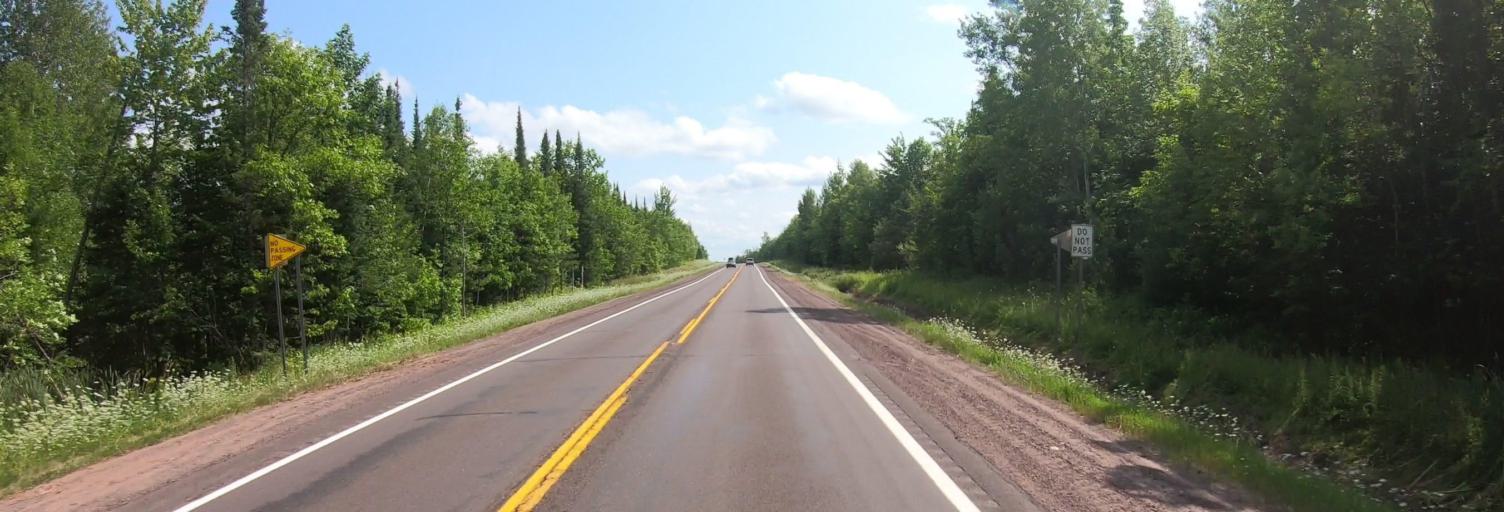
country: US
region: Michigan
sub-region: Ontonagon County
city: Ontonagon
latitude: 46.8256
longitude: -88.9972
